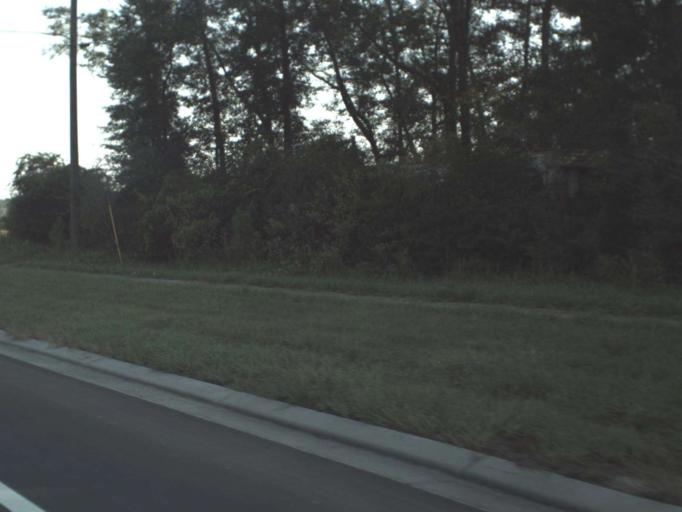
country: US
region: Florida
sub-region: Bay County
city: Laguna Beach
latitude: 30.4516
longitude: -85.8736
